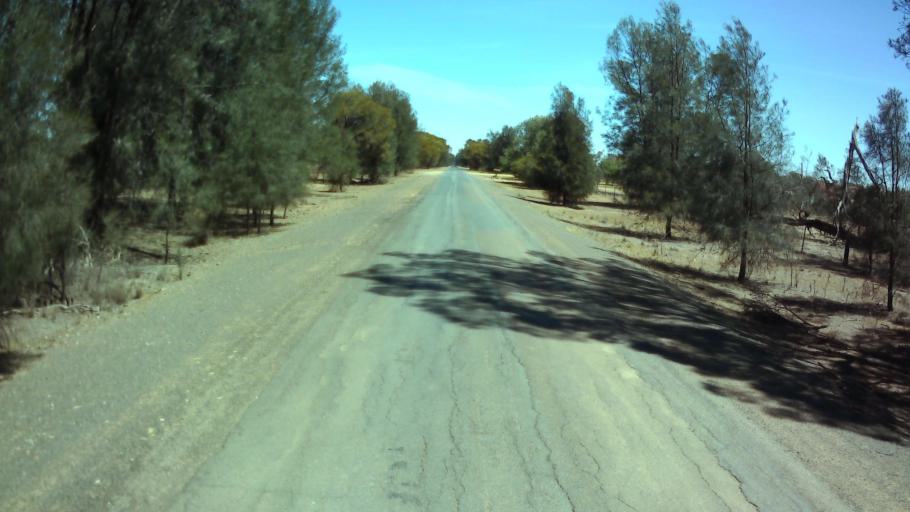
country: AU
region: New South Wales
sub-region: Weddin
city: Grenfell
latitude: -33.8694
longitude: 147.6922
